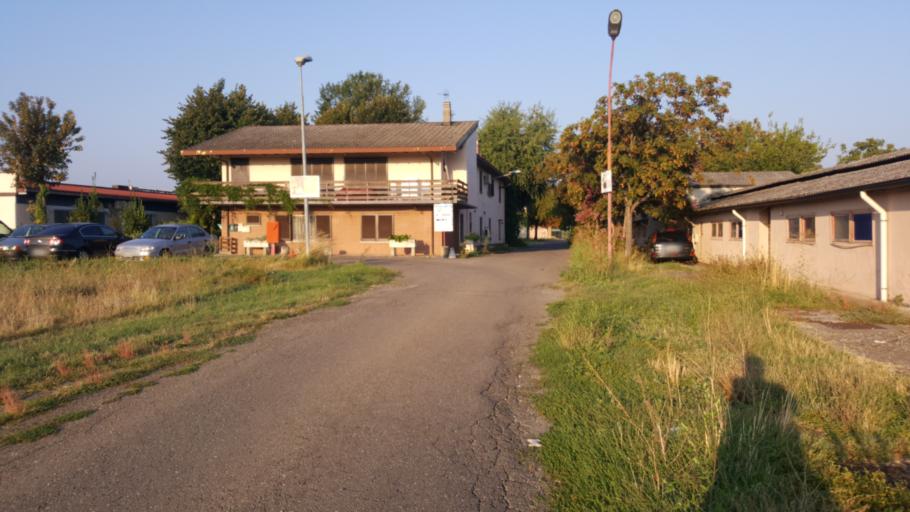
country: IT
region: Lombardy
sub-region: Provincia di Pavia
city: Rivanazzano
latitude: 44.9515
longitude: 9.0142
